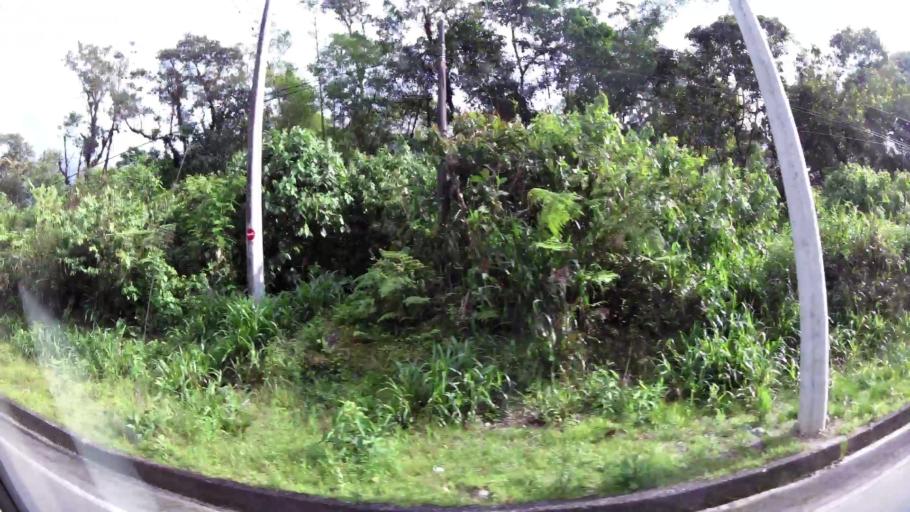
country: EC
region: Pastaza
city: Puyo
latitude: -1.4116
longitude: -78.1961
